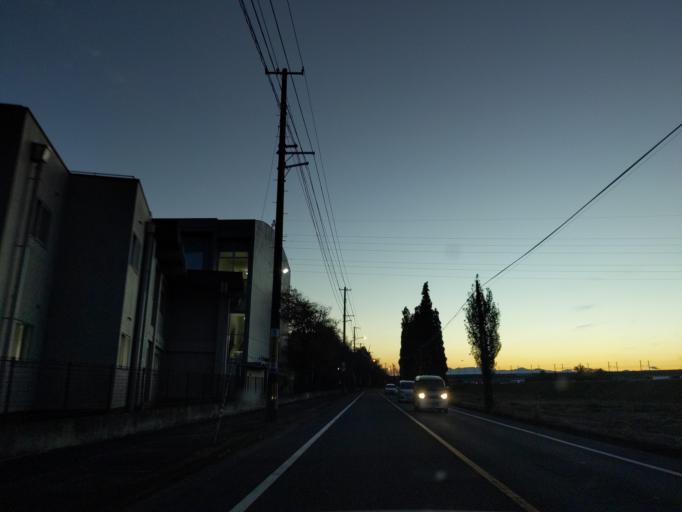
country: JP
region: Fukushima
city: Koriyama
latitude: 37.3617
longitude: 140.3817
